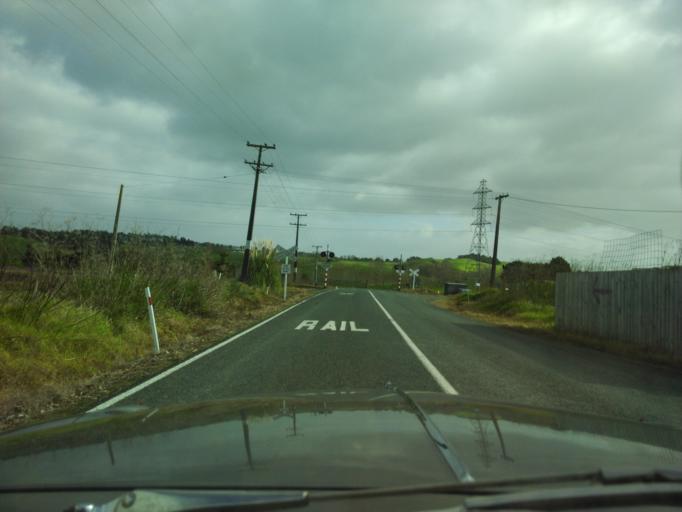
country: NZ
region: Auckland
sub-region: Auckland
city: Wellsford
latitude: -36.1647
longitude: 174.4290
